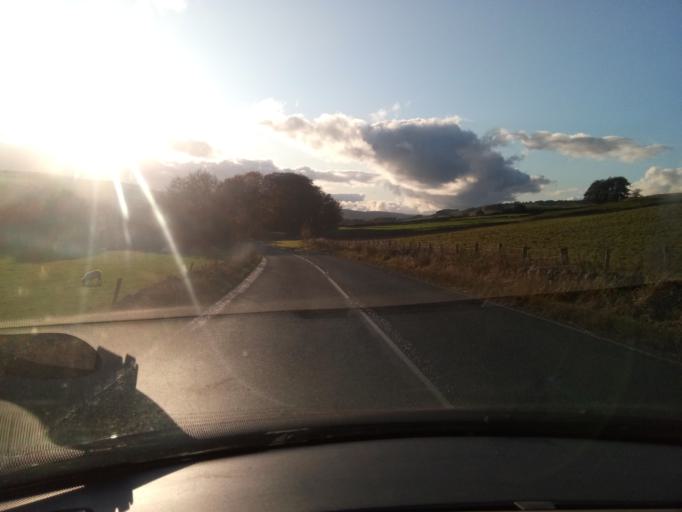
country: GB
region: England
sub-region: County Durham
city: Stanhope
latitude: 54.7453
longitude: -2.0578
